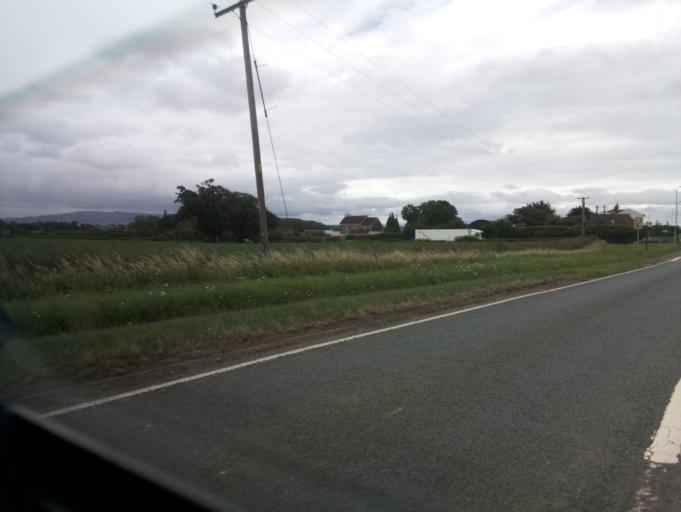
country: GB
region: England
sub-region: Worcestershire
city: Upton upon Severn
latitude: 52.0723
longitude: -2.1995
